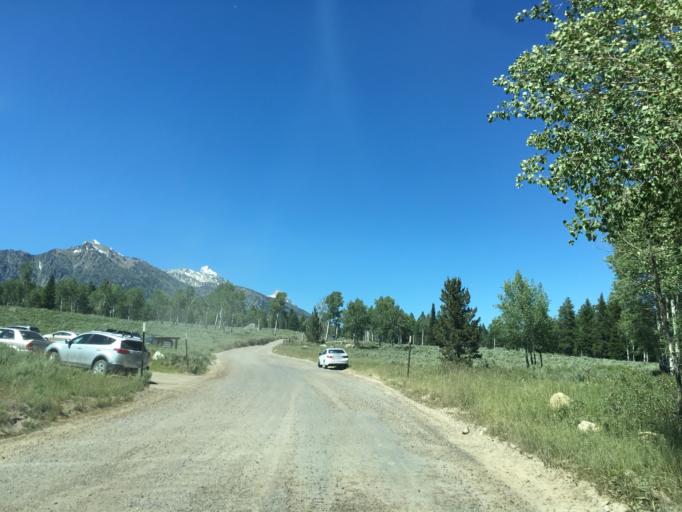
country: US
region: Wyoming
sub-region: Teton County
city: Moose Wilson Road
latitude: 43.6069
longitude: -110.7928
